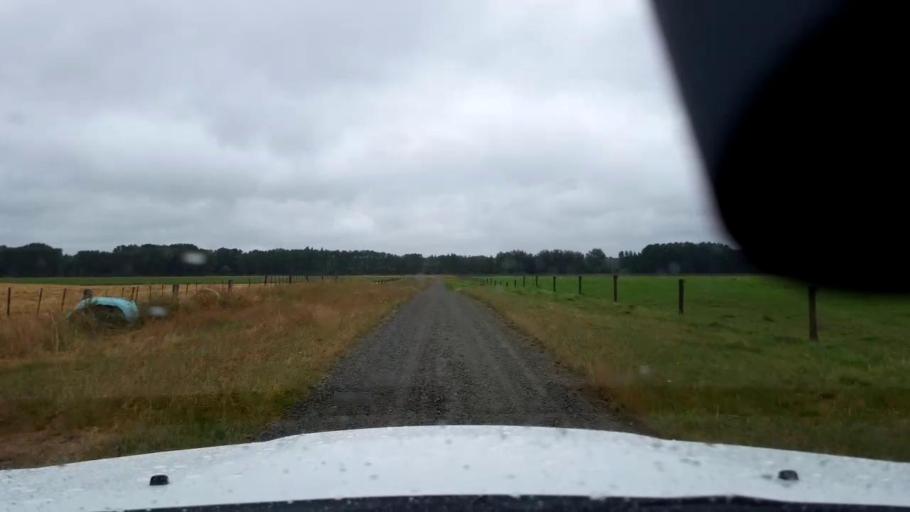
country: NZ
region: Canterbury
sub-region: Timaru District
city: Pleasant Point
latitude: -44.2540
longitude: 171.2000
